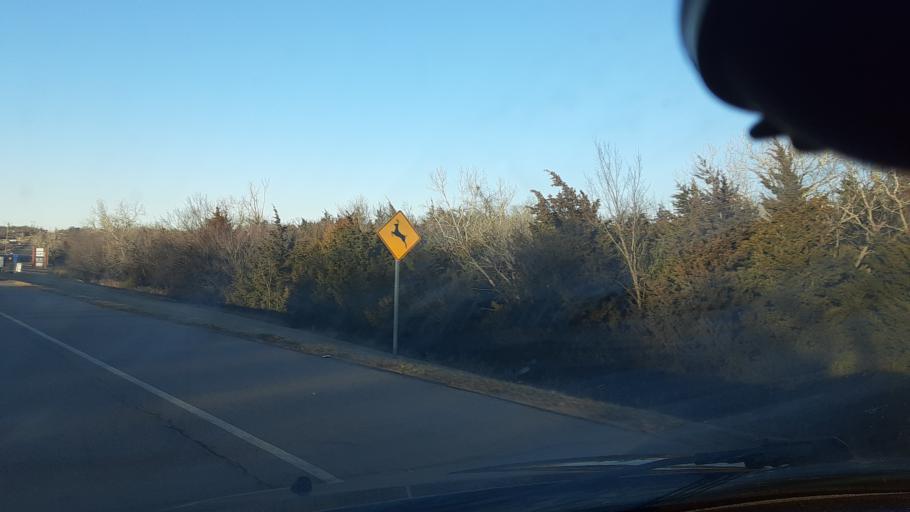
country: US
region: Oklahoma
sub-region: Logan County
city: Guthrie
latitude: 35.8307
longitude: -97.4251
